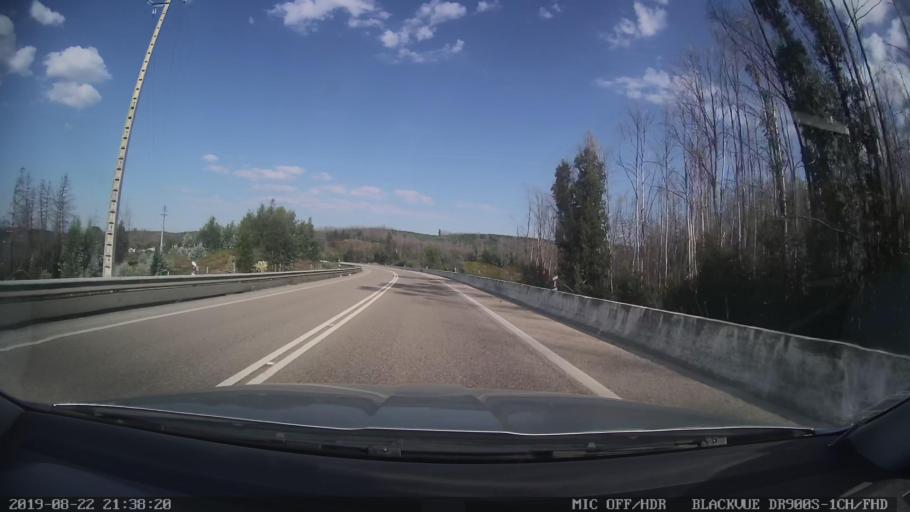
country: PT
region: Leiria
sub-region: Figueiro Dos Vinhos
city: Figueiro dos Vinhos
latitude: 39.9357
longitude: -8.2662
